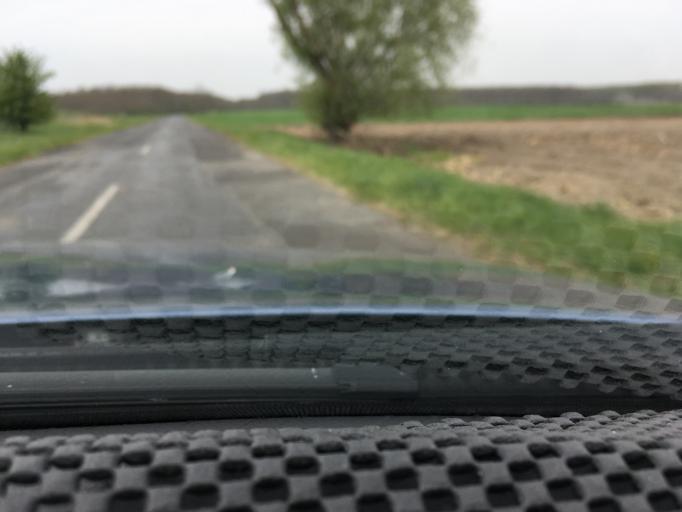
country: HU
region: Szabolcs-Szatmar-Bereg
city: Nyirmihalydi
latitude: 47.6913
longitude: 21.9683
